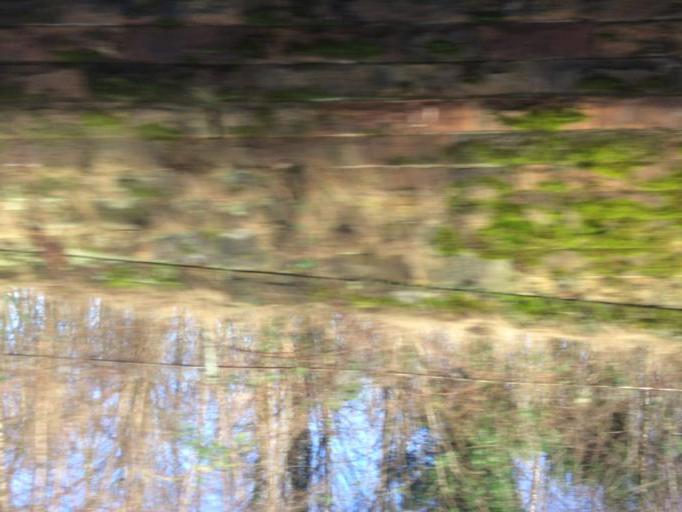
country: GB
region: Scotland
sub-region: Glasgow City
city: Glasgow
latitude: 55.8288
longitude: -4.2595
